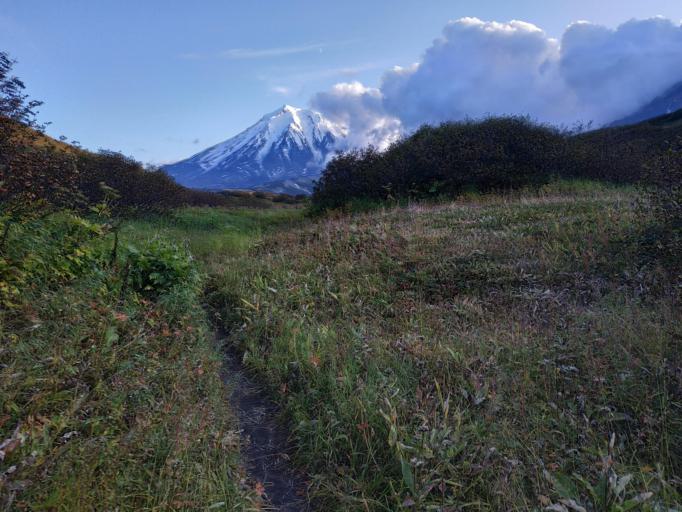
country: RU
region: Kamtsjatka
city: Petropavlovsk-Kamchatsky
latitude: 53.4330
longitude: 158.7287
